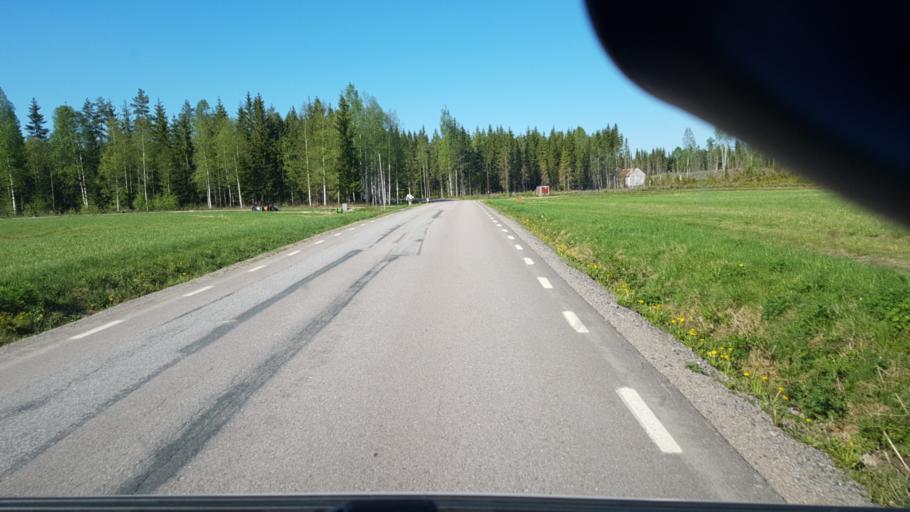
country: SE
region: Vaermland
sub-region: Eda Kommun
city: Charlottenberg
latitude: 59.8740
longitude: 12.3500
